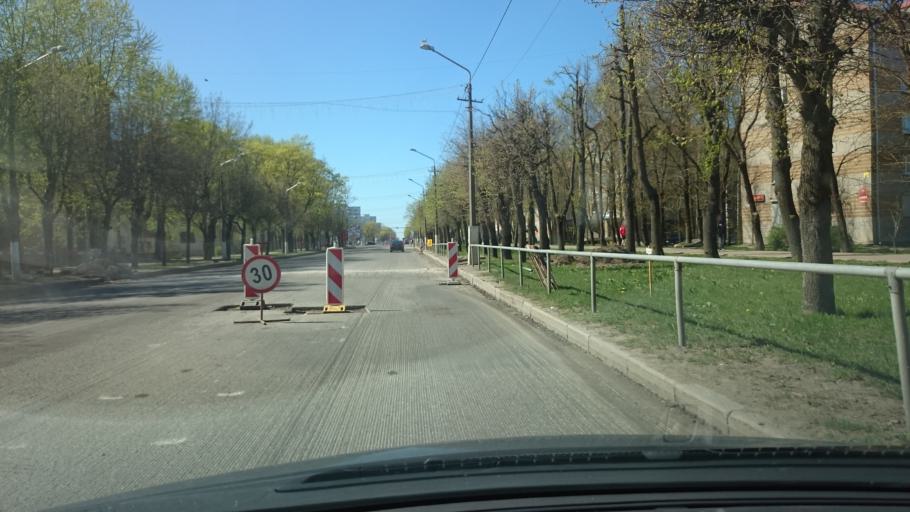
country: EE
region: Ida-Virumaa
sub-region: Narva linn
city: Narva
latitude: 59.3786
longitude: 28.1843
